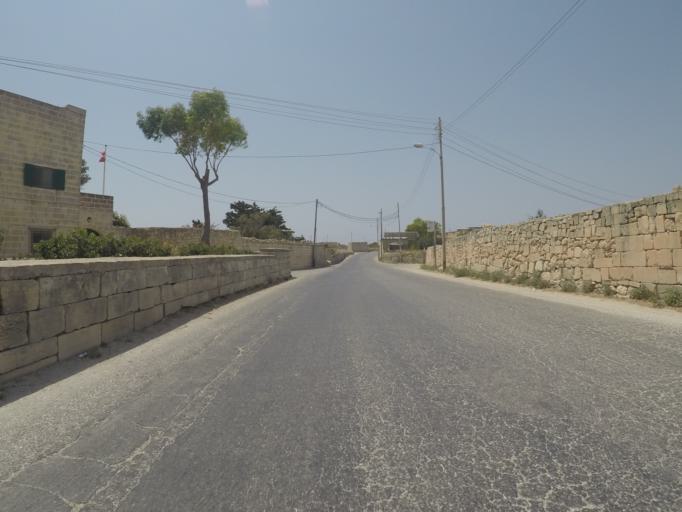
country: MT
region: Is-Siggiewi
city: Siggiewi
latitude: 35.8414
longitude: 14.4327
